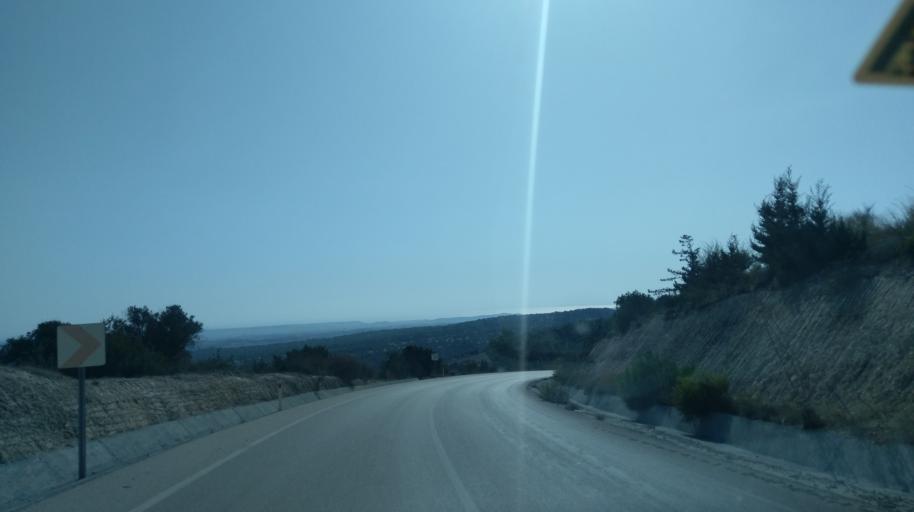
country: CY
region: Ammochostos
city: Leonarisso
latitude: 35.4275
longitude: 33.9792
